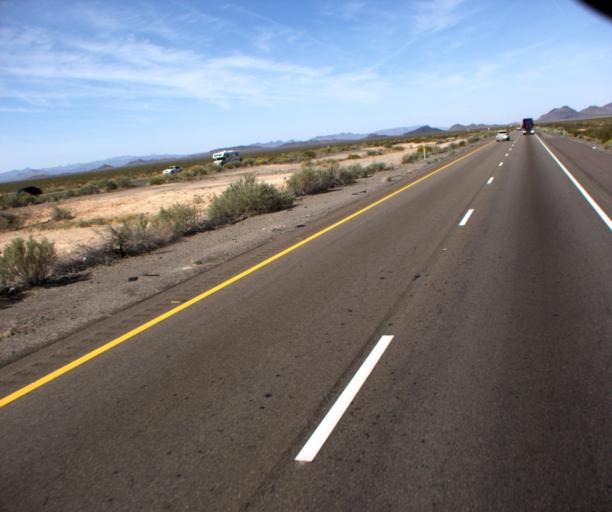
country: US
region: Arizona
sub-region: La Paz County
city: Salome
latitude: 33.5962
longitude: -113.5319
